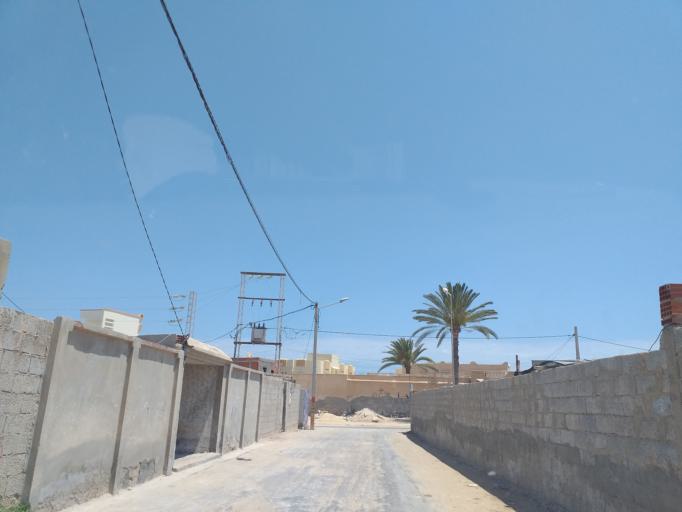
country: TN
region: Qabis
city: Gabes
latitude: 33.9430
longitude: 10.0594
